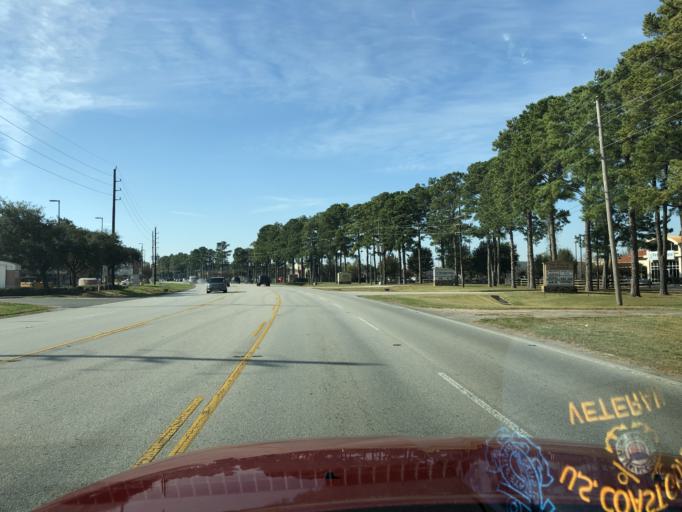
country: US
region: Texas
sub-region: Harris County
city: Tomball
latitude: 30.0356
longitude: -95.5532
